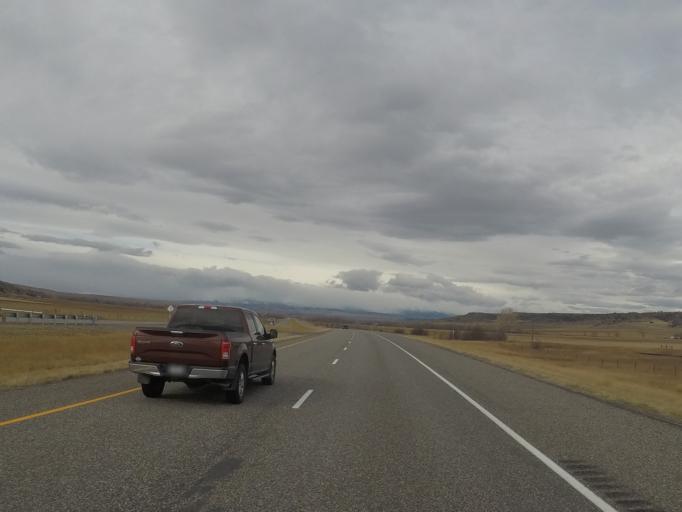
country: US
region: Montana
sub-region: Sweet Grass County
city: Big Timber
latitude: 45.7792
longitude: -109.8036
